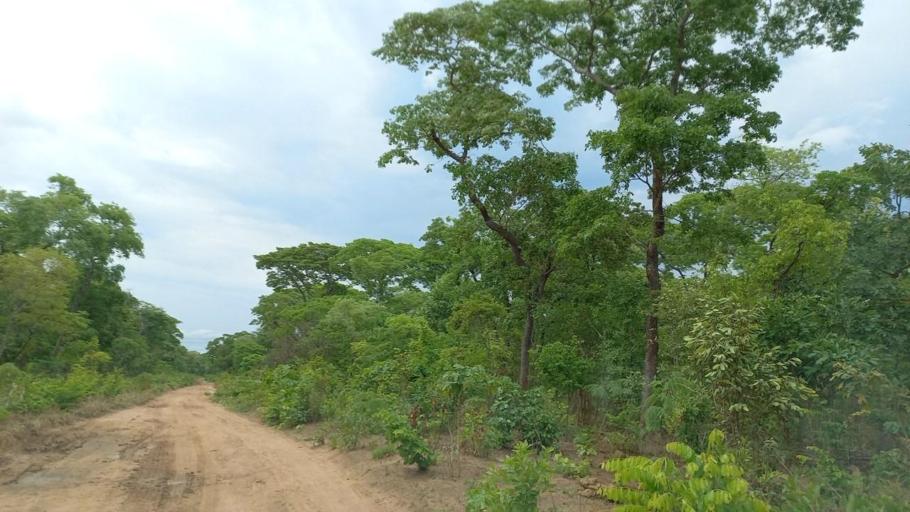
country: ZM
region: North-Western
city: Kalengwa
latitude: -13.5497
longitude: 24.9758
